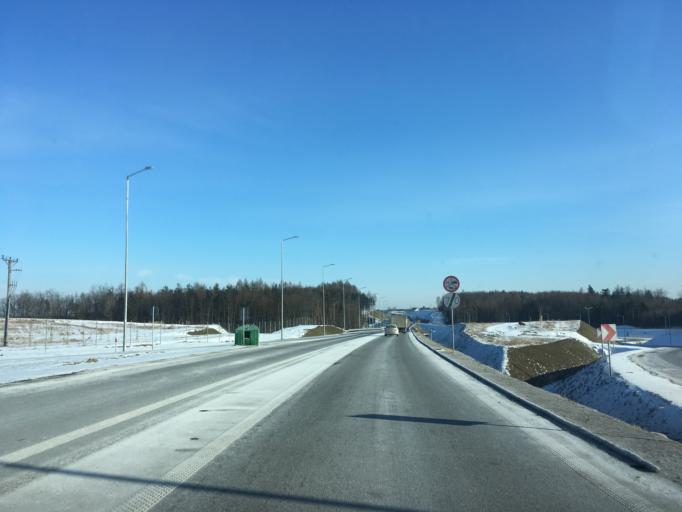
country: PL
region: Pomeranian Voivodeship
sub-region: Powiat koscierski
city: Koscierzyna
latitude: 54.1127
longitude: 17.9505
